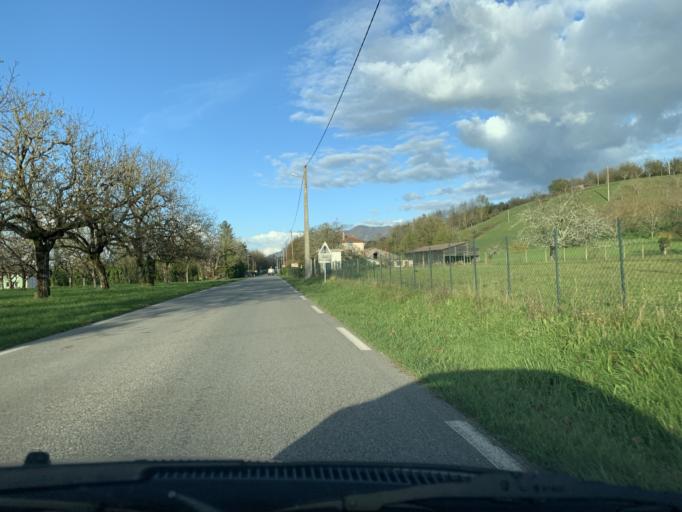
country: FR
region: Rhone-Alpes
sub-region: Departement de la Drome
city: Saint-Jean-en-Royans
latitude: 45.0261
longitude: 5.2979
